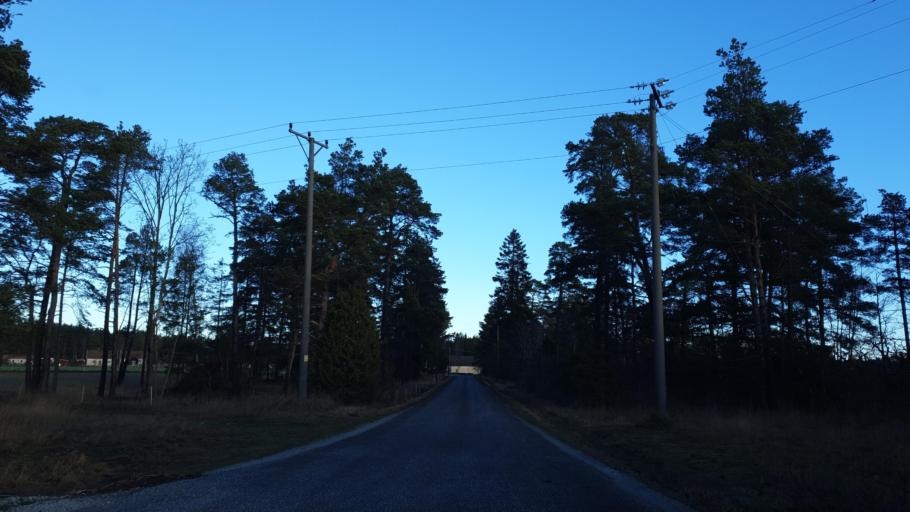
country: SE
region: Gotland
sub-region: Gotland
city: Slite
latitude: 57.3821
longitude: 18.8072
